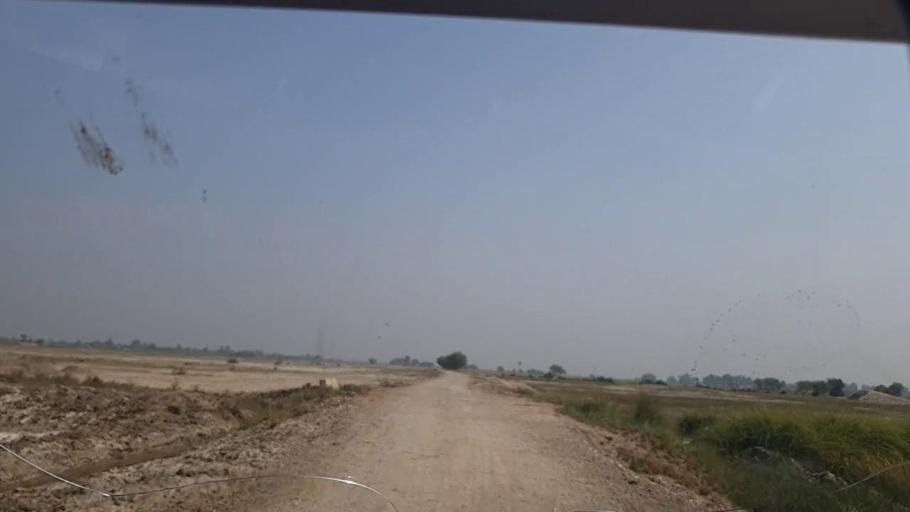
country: PK
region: Sindh
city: Shikarpur
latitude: 28.0513
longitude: 68.6634
